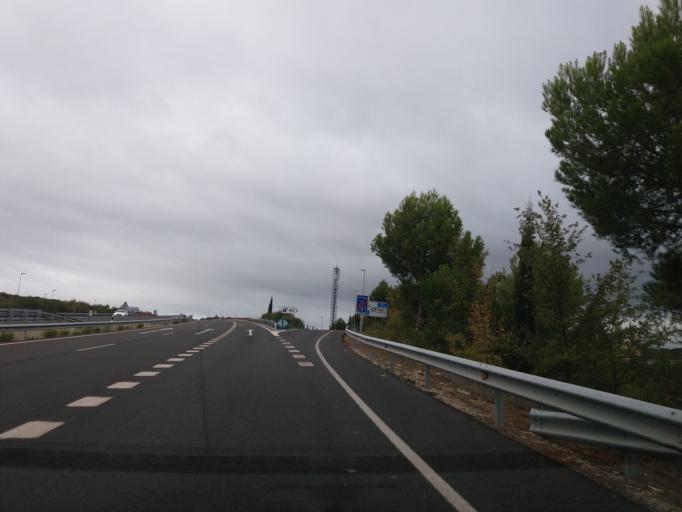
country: ES
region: Navarre
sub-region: Provincia de Navarra
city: Ayegui
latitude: 42.6501
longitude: -2.0215
